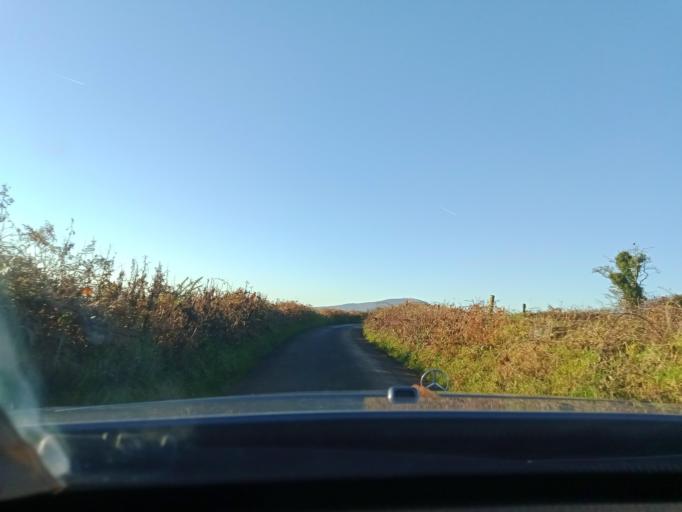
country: IE
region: Leinster
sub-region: Kilkenny
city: Callan
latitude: 52.4611
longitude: -7.4178
